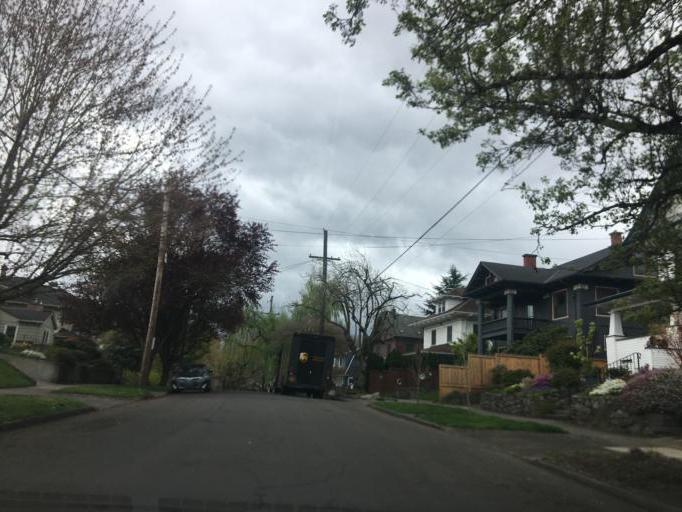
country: US
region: Oregon
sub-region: Multnomah County
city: Portland
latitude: 45.5276
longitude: -122.6267
